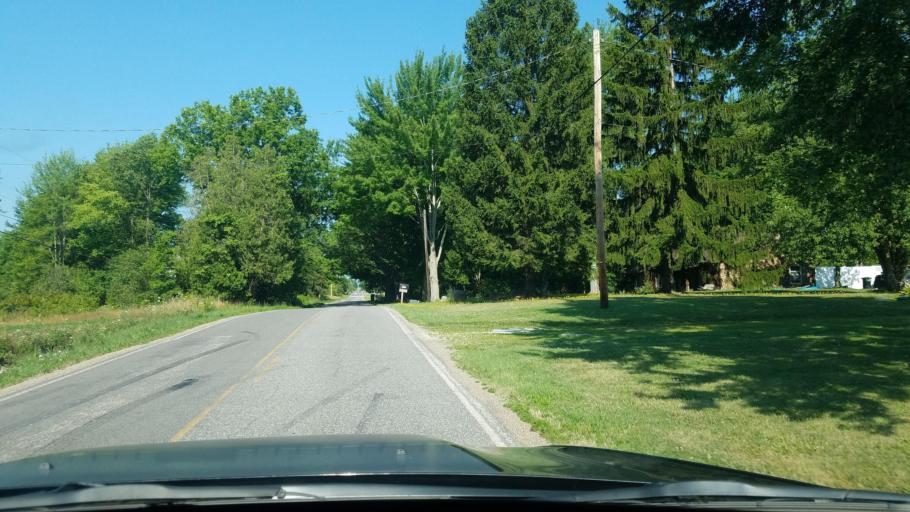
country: US
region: Ohio
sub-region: Trumbull County
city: Leavittsburg
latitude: 41.2795
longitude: -80.9175
